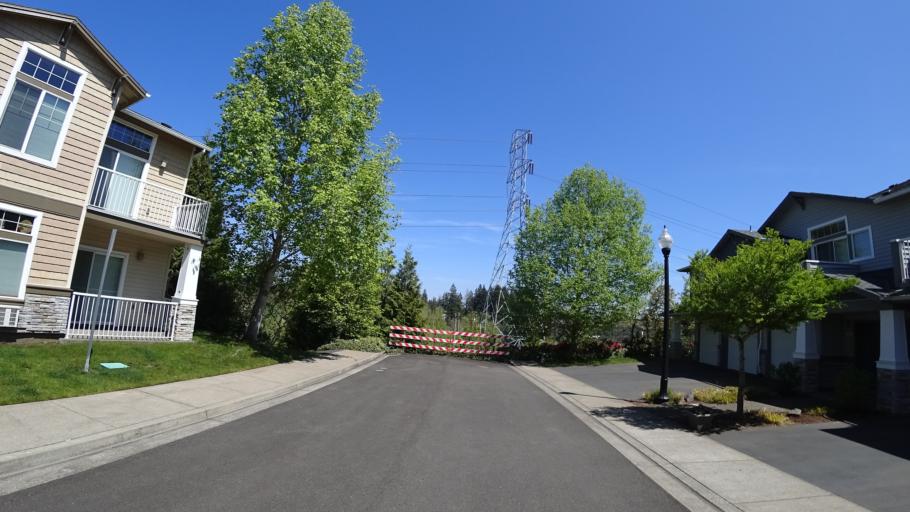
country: US
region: Oregon
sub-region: Washington County
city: King City
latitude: 45.4324
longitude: -122.8283
